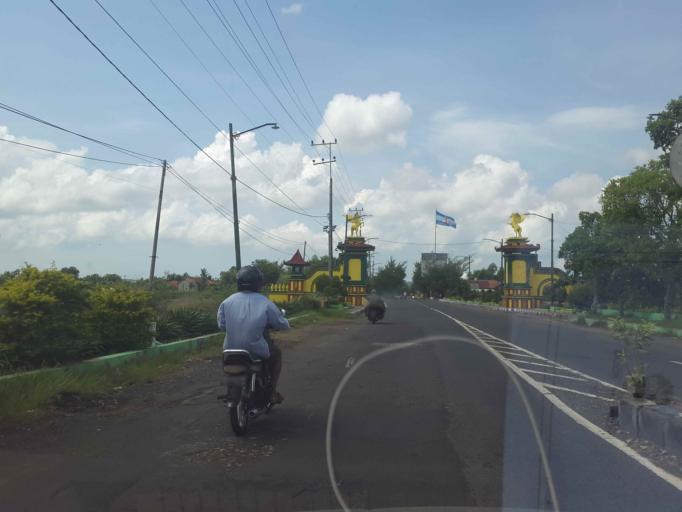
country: ID
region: East Java
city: Palebunan
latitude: -7.0496
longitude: 113.8441
